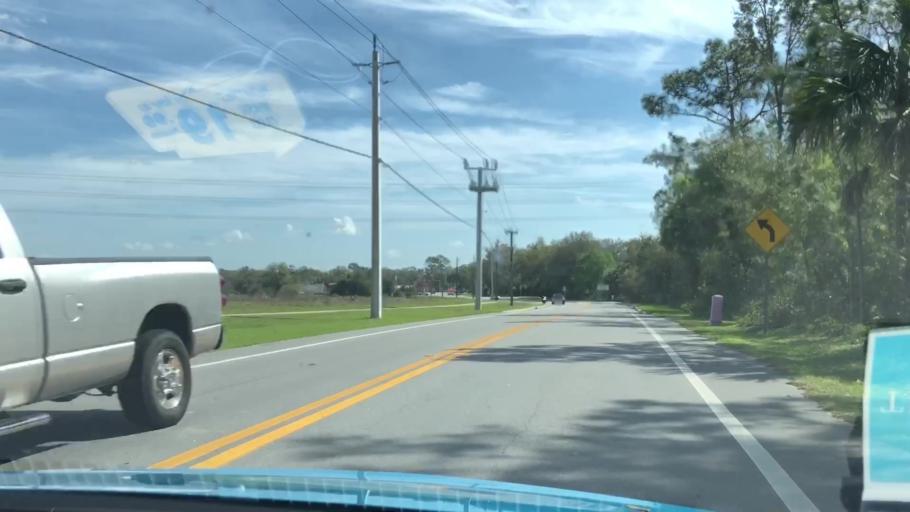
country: US
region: Florida
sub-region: Seminole County
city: Midway
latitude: 28.8506
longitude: -81.1669
